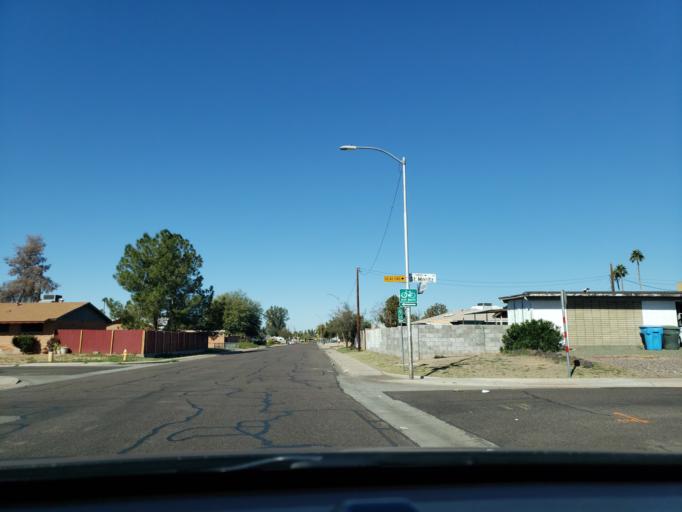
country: US
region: Arizona
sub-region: Maricopa County
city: Glendale
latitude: 33.6195
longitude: -112.1217
